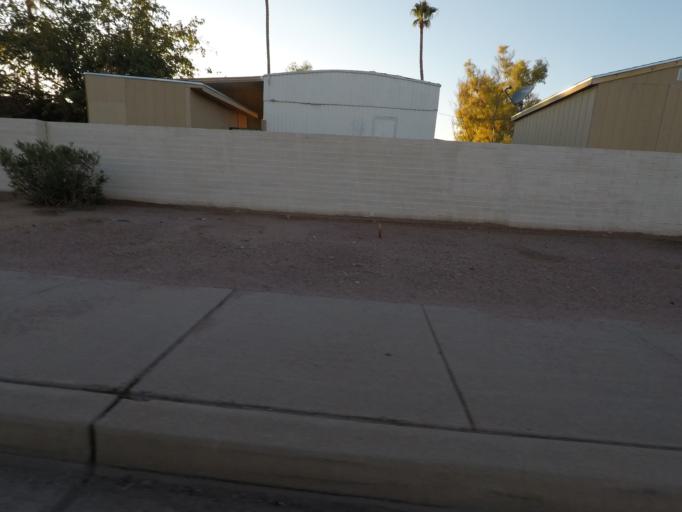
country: US
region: Arizona
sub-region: Maricopa County
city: Guadalupe
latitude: 33.3815
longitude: -111.9439
